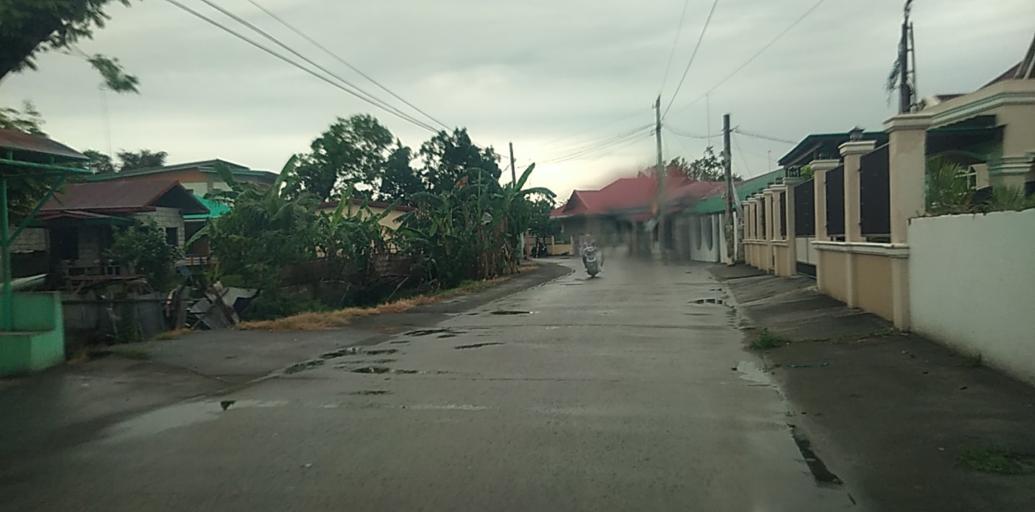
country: PH
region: Central Luzon
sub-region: Province of Pampanga
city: Arayat
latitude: 15.1408
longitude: 120.7347
